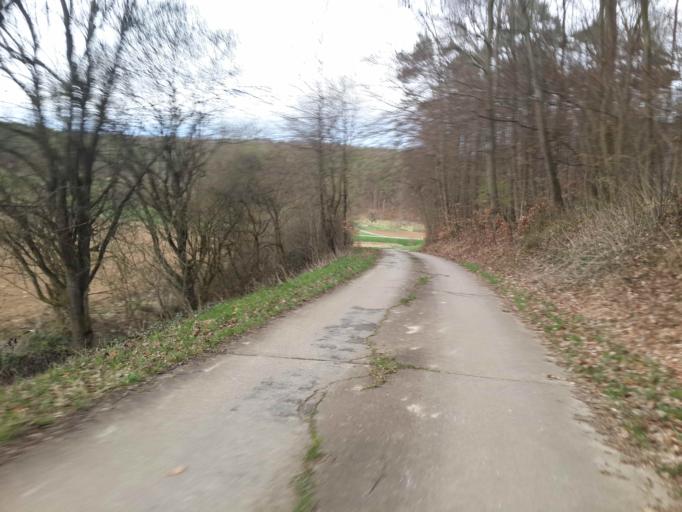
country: DE
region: Baden-Wuerttemberg
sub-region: Regierungsbezirk Stuttgart
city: Buch am Ahorn
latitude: 49.5016
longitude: 9.5708
